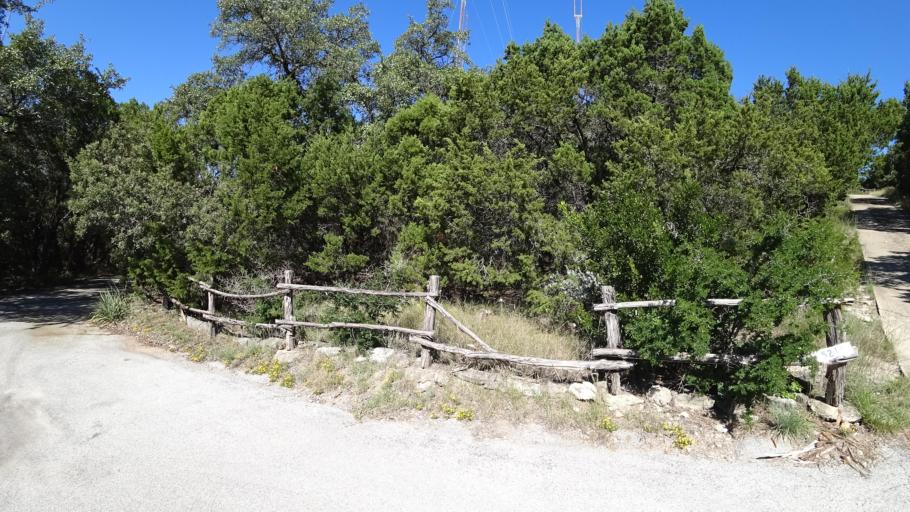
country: US
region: Texas
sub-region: Travis County
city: West Lake Hills
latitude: 30.3217
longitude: -97.7975
